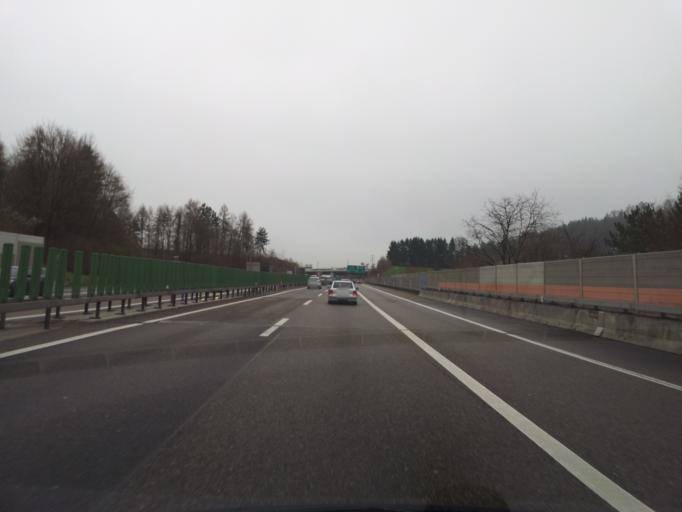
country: CH
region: Zurich
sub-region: Bezirk Winterthur
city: Wuelflingen (Kreis 6) / Lindenplatz
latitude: 47.5144
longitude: 8.6913
